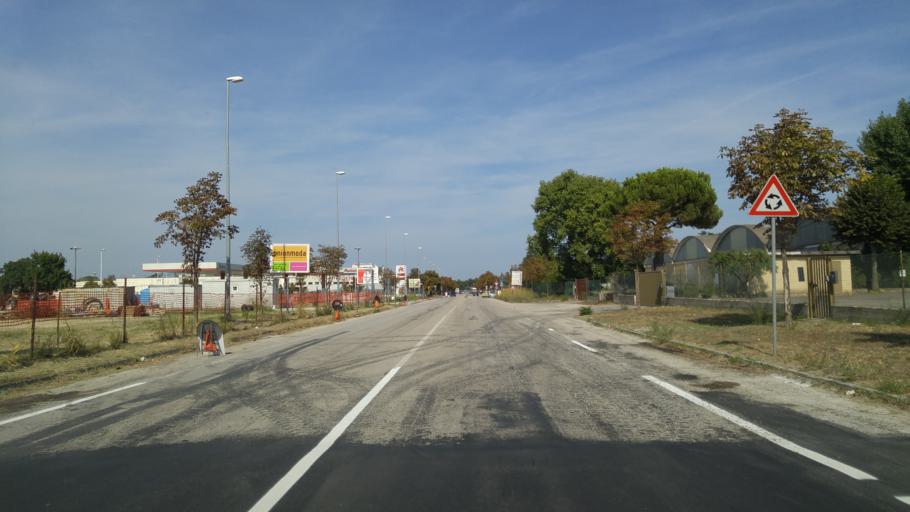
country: IT
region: The Marches
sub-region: Provincia di Pesaro e Urbino
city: Bellocchi
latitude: 43.7981
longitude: 13.0100
